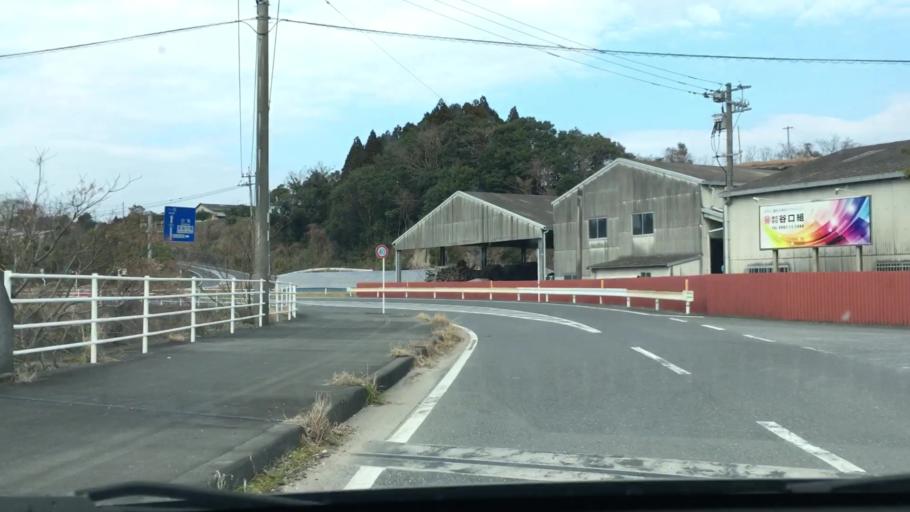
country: JP
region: Miyazaki
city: Kushima
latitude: 31.4999
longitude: 131.2387
